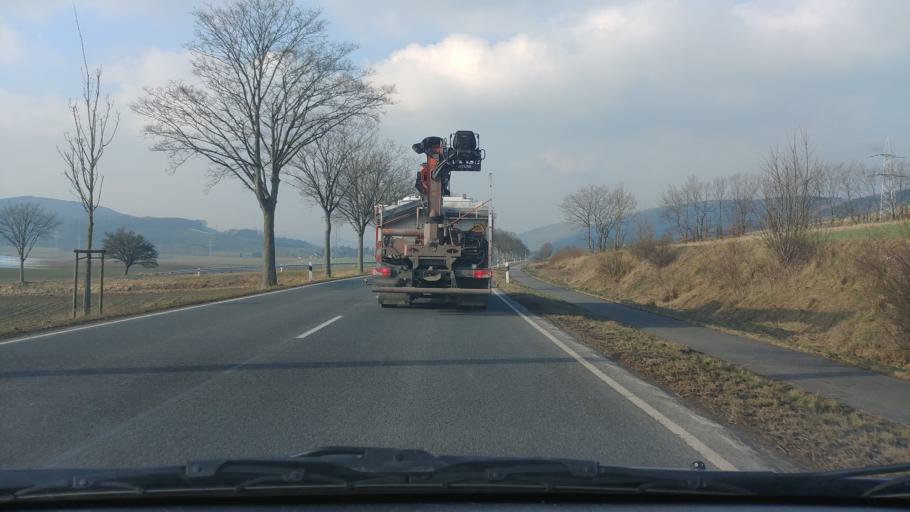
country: DE
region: Lower Saxony
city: Freden
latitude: 51.8958
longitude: 9.8724
